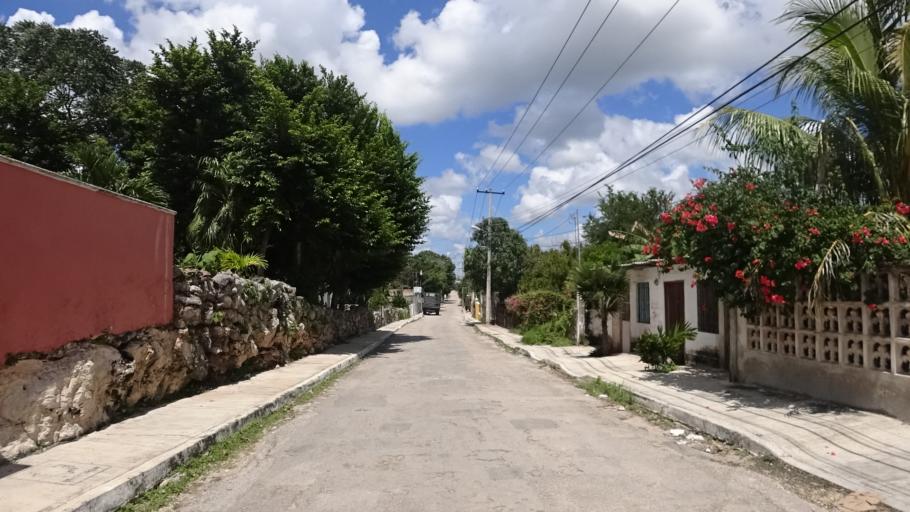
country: MX
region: Yucatan
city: Valladolid
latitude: 20.6831
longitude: -88.2132
